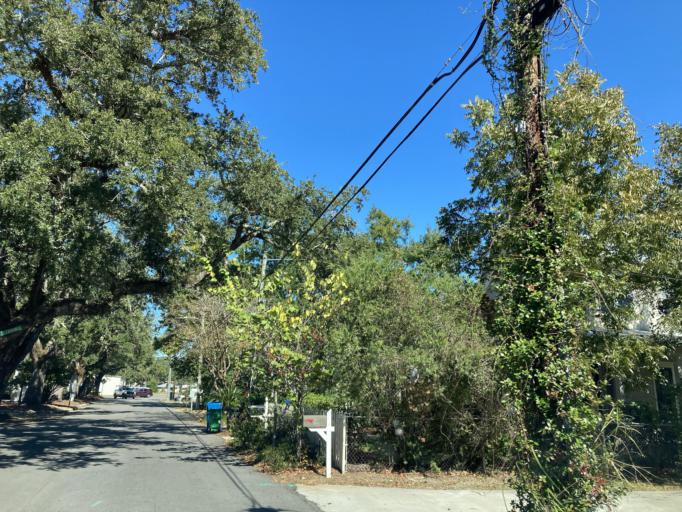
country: US
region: Mississippi
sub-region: Jackson County
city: Ocean Springs
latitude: 30.4104
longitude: -88.8264
